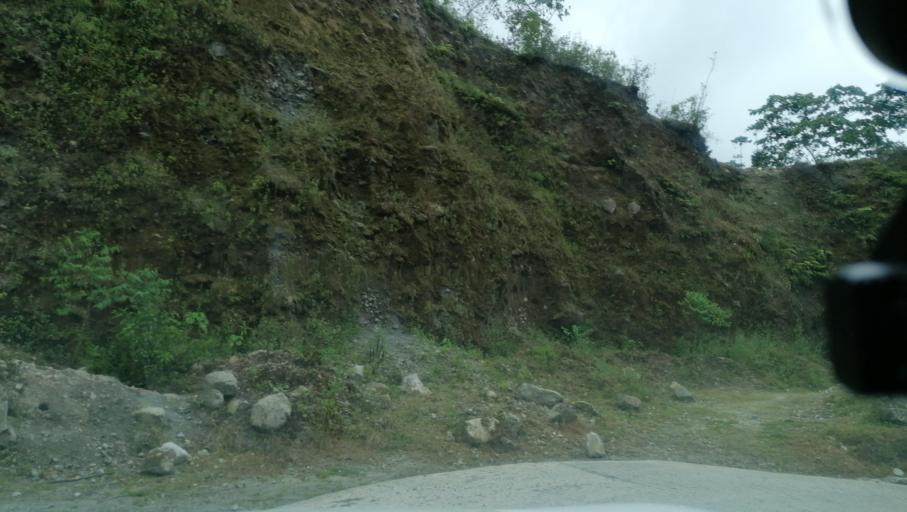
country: MX
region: Chiapas
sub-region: Cacahoatan
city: Benito Juarez
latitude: 15.0897
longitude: -92.1595
